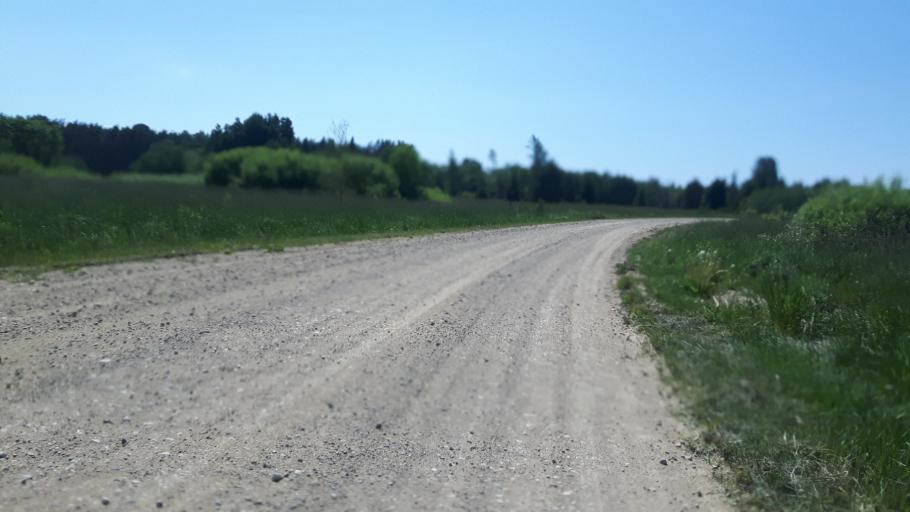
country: EE
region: Paernumaa
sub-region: Vaendra vald (alev)
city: Vandra
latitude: 58.5546
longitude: 24.9508
